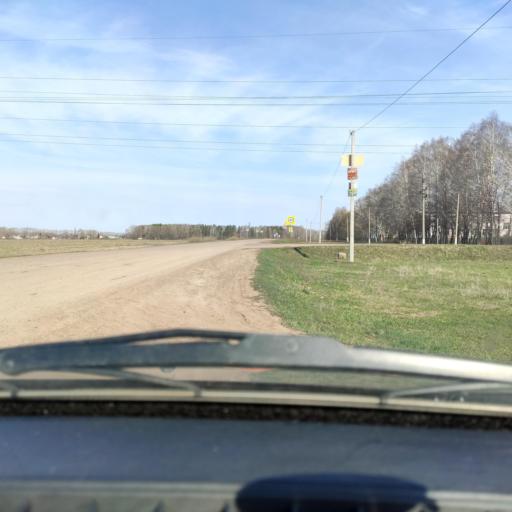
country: RU
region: Bashkortostan
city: Asanovo
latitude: 54.7658
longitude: 55.4868
